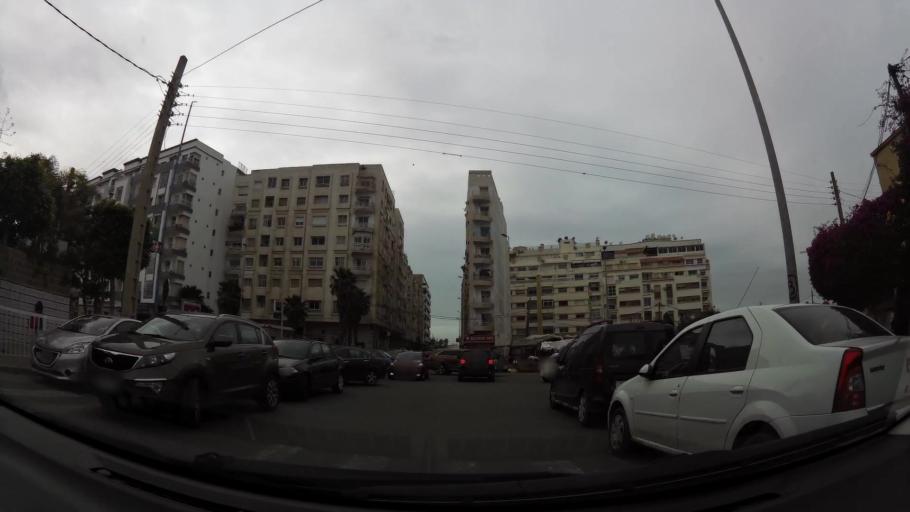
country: MA
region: Grand Casablanca
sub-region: Casablanca
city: Casablanca
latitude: 33.5948
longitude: -7.6507
